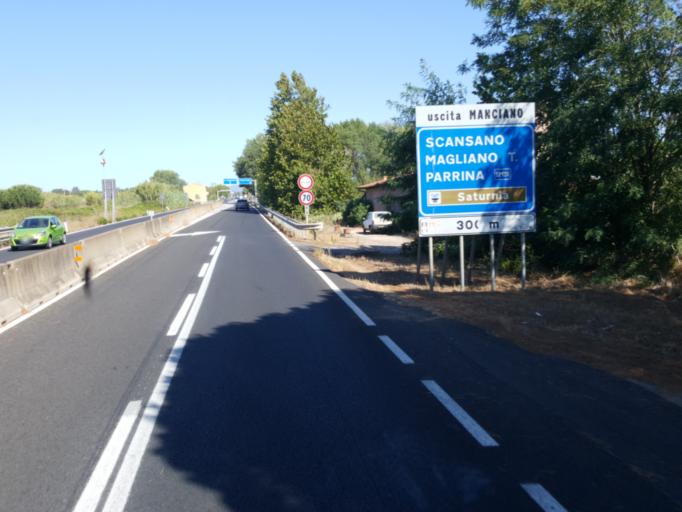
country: IT
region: Tuscany
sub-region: Provincia di Grosseto
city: Orbetello Scalo
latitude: 42.4694
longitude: 11.2377
